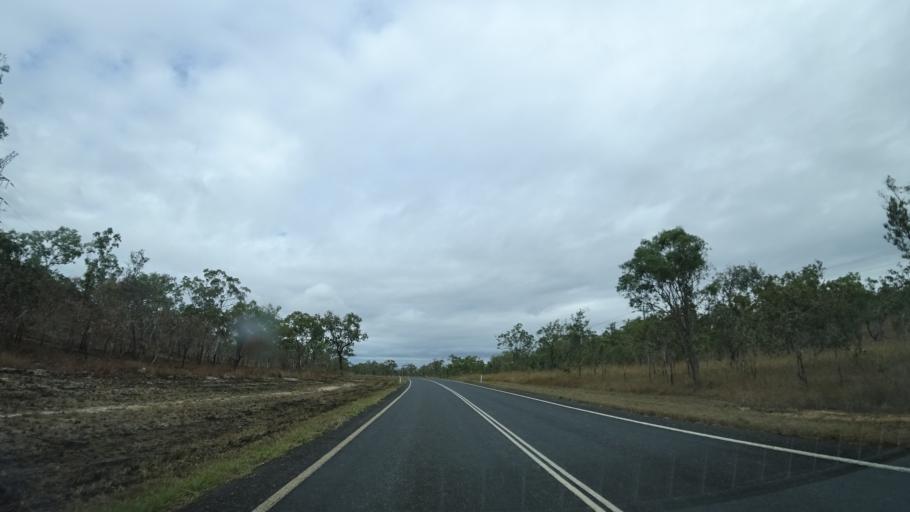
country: AU
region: Queensland
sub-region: Tablelands
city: Mareeba
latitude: -16.7760
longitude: 145.3403
